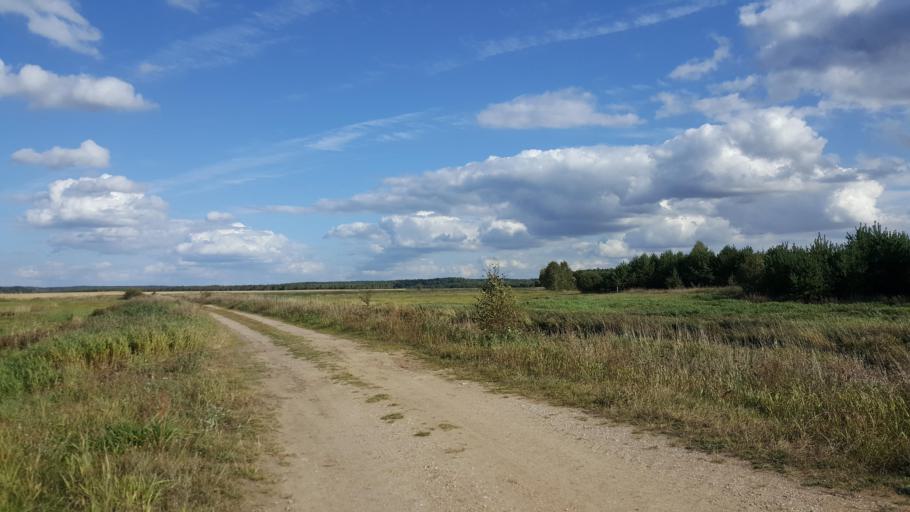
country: BY
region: Brest
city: Kamyanyets
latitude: 52.4448
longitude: 23.9347
